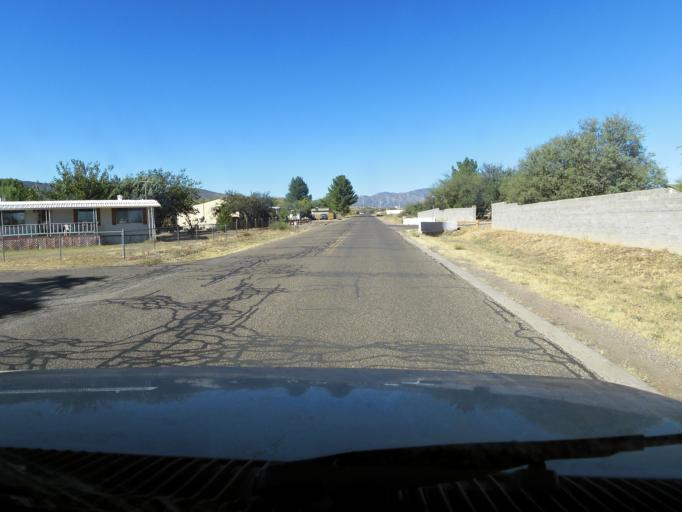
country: US
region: Arizona
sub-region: Yavapai County
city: Camp Verde
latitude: 34.5985
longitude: -111.8898
